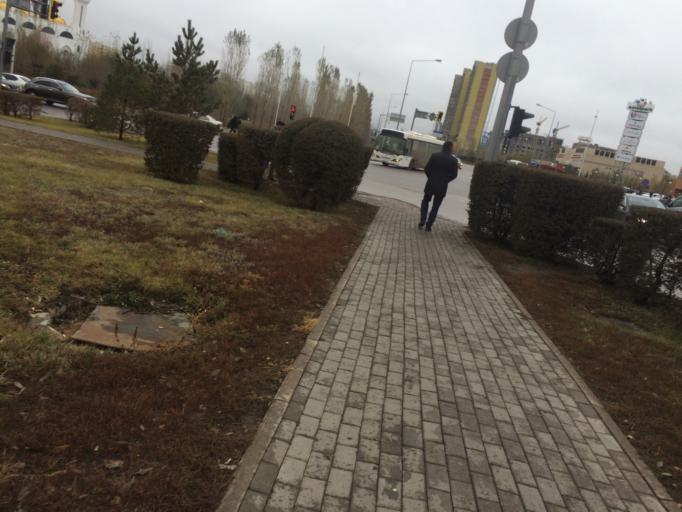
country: KZ
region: Astana Qalasy
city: Astana
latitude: 51.1280
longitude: 71.4139
